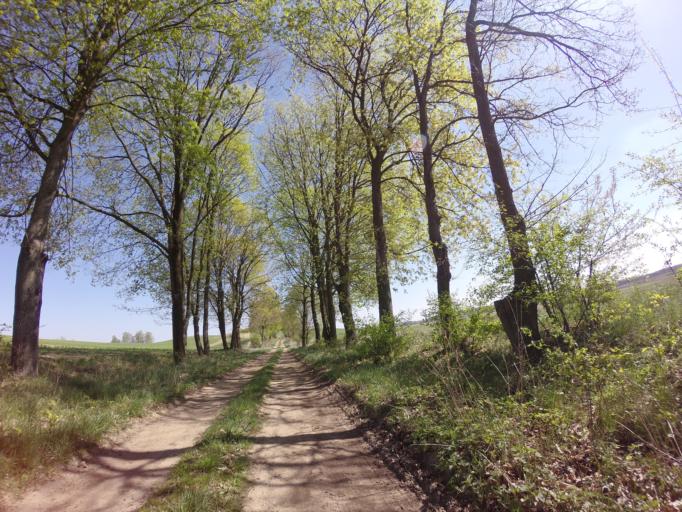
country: PL
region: West Pomeranian Voivodeship
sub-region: Powiat choszczenski
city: Choszczno
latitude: 53.1800
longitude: 15.3699
